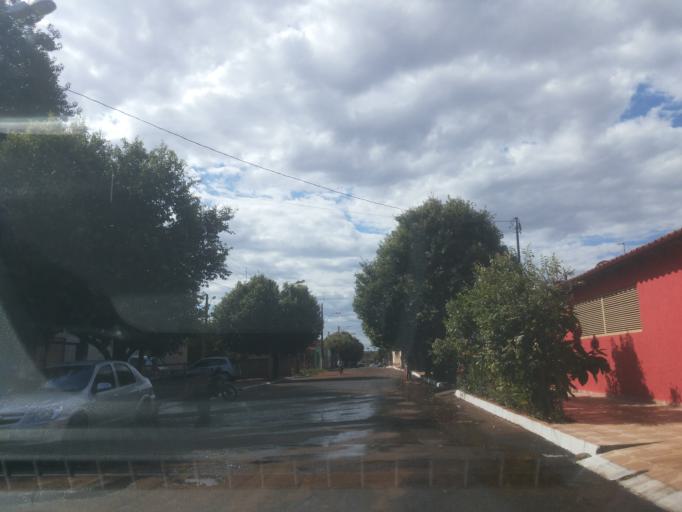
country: BR
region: Goias
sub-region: Itumbiara
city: Itumbiara
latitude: -18.4384
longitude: -49.1870
